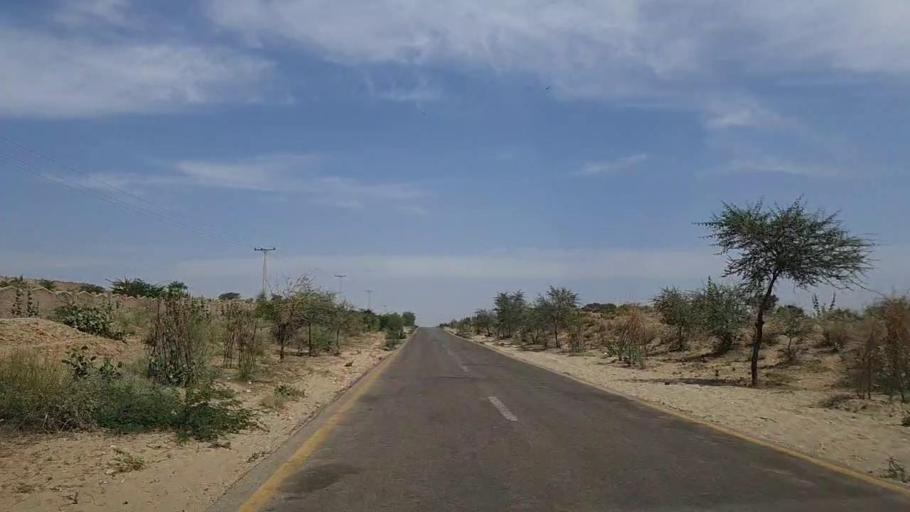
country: PK
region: Sindh
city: Mithi
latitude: 24.7705
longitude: 69.8004
